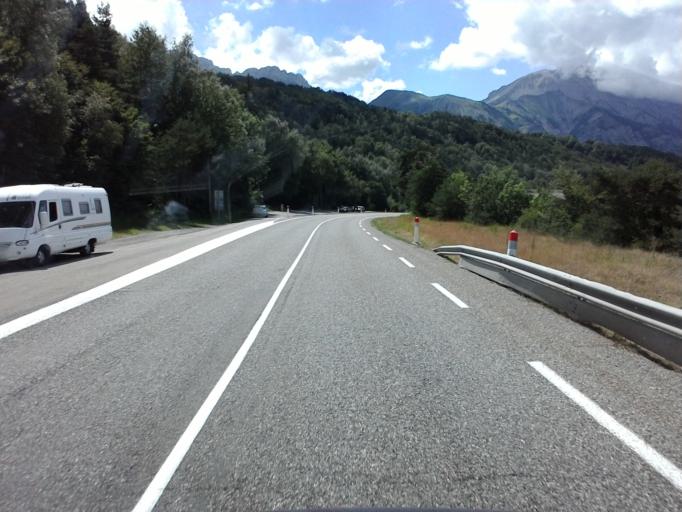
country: FR
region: Provence-Alpes-Cote d'Azur
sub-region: Departement des Hautes-Alpes
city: Saint-Bonnet-en-Champsaur
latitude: 44.7004
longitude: 6.0544
